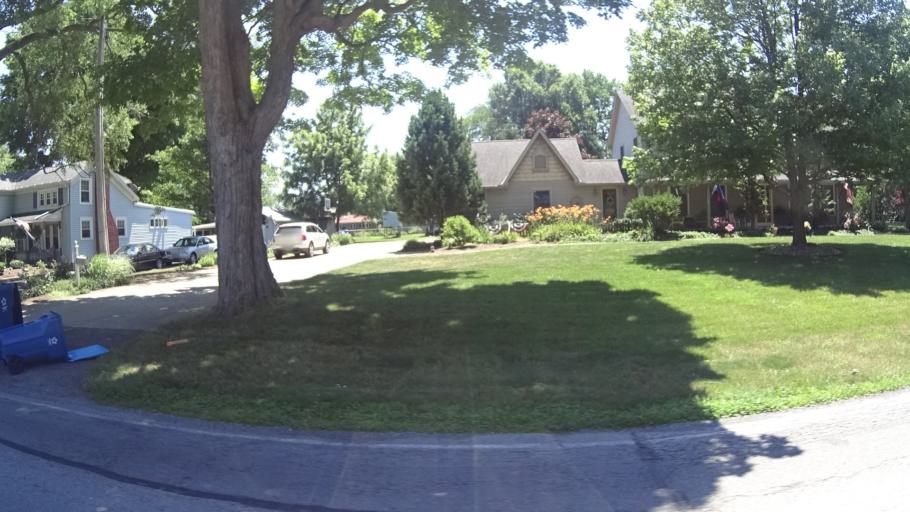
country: US
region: Ohio
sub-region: Erie County
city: Huron
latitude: 41.3888
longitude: -82.5630
